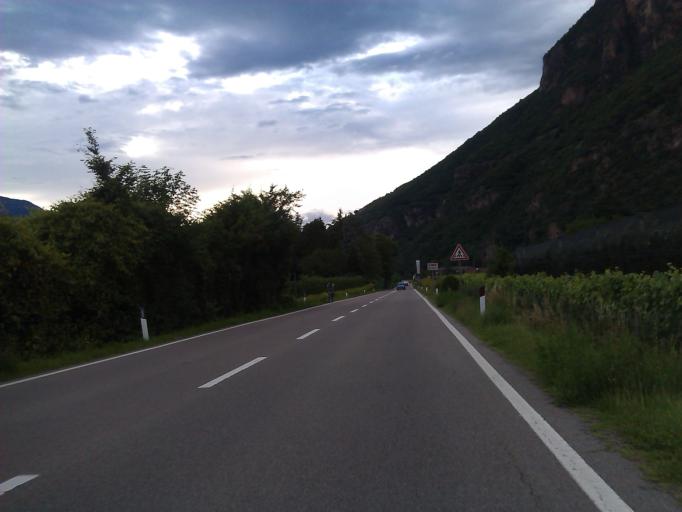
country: IT
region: Trentino-Alto Adige
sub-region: Bolzano
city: Bolzano
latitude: 46.4996
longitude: 11.3019
